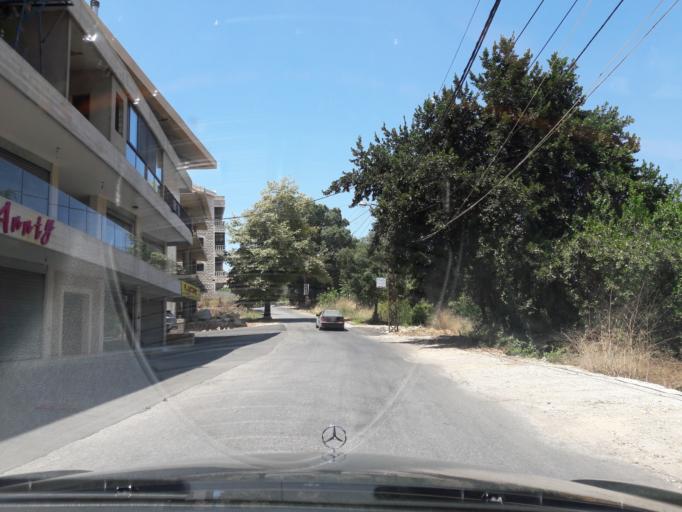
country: LB
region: Mont-Liban
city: Djounie
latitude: 33.9256
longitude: 35.6683
